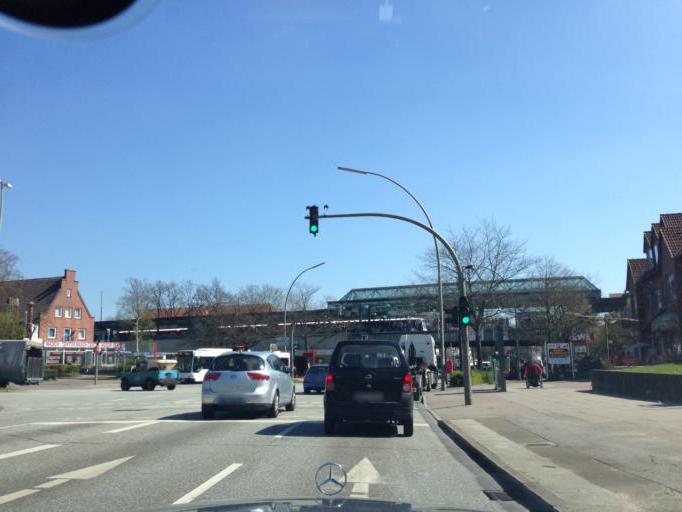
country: DE
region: Hamburg
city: Farmsen-Berne
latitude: 53.6073
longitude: 10.1163
